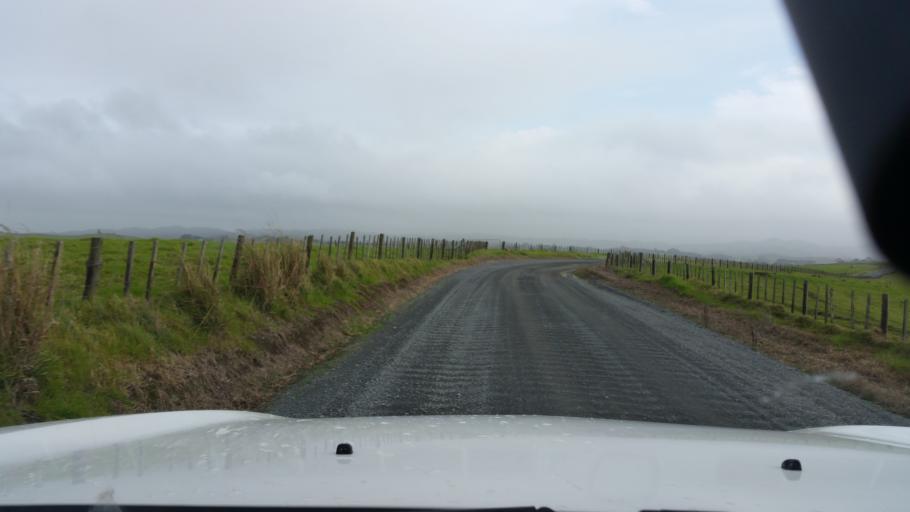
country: NZ
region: Northland
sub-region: Whangarei
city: Ngunguru
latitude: -35.7660
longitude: 174.5274
